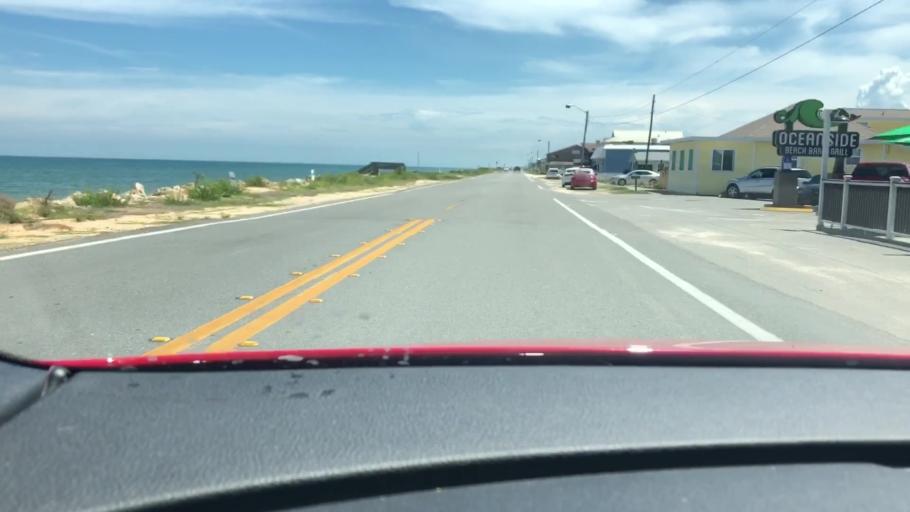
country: US
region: Florida
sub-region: Flagler County
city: Flagler Beach
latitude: 29.4624
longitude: -81.1185
